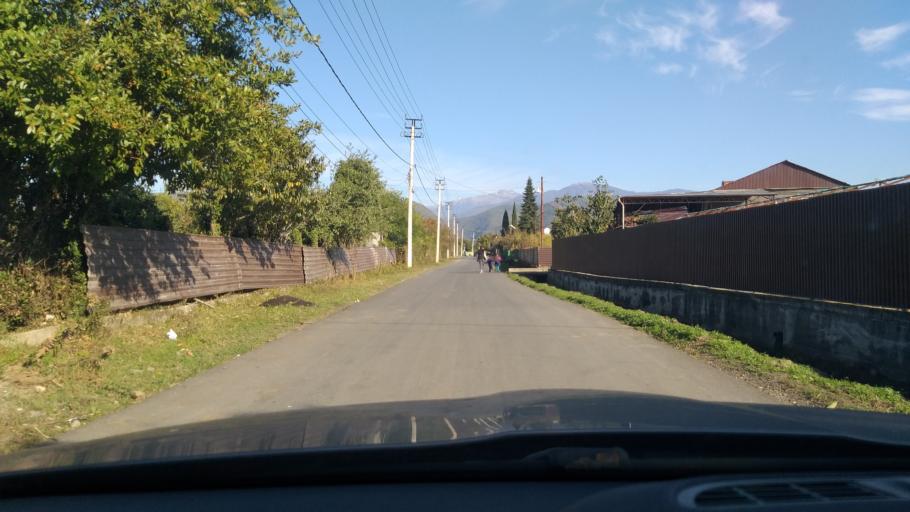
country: GE
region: Abkhazia
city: Sokhumi
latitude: 43.0163
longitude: 40.9647
